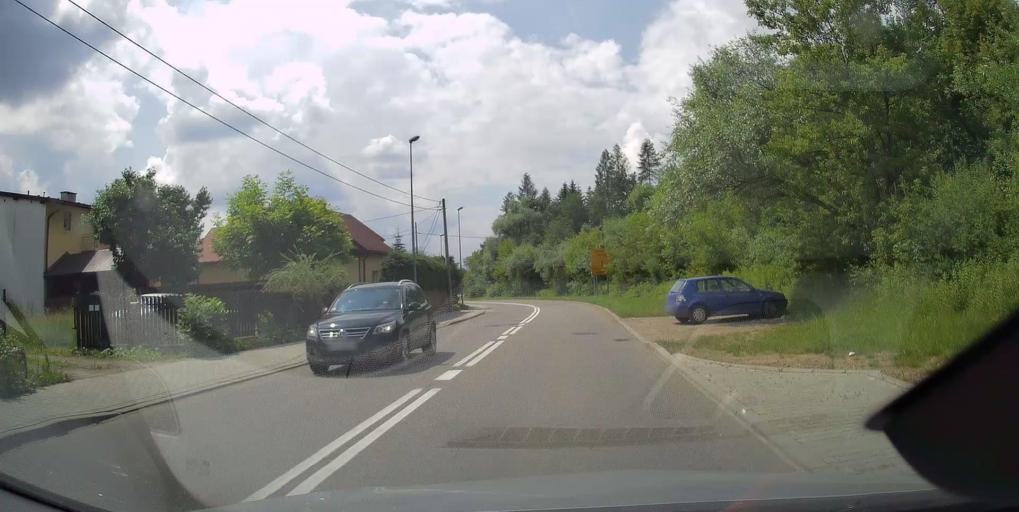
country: PL
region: Lesser Poland Voivodeship
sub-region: Powiat nowosadecki
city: Nowy Sacz
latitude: 49.6351
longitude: 20.7128
